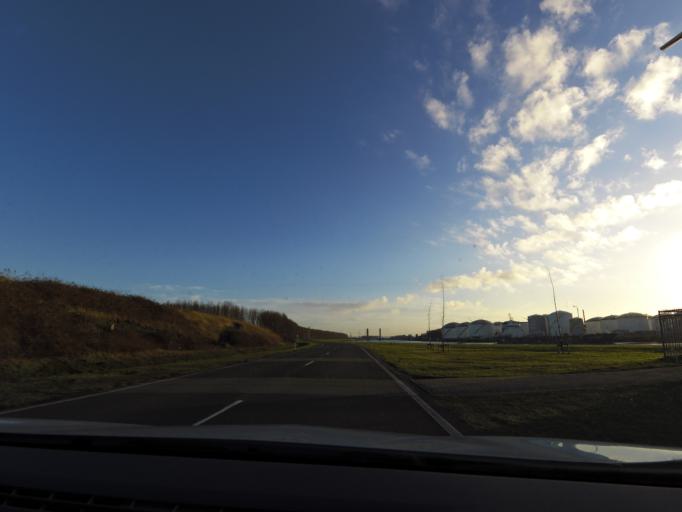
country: NL
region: South Holland
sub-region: Gemeente Maassluis
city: Maassluis
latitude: 51.9185
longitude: 4.2215
